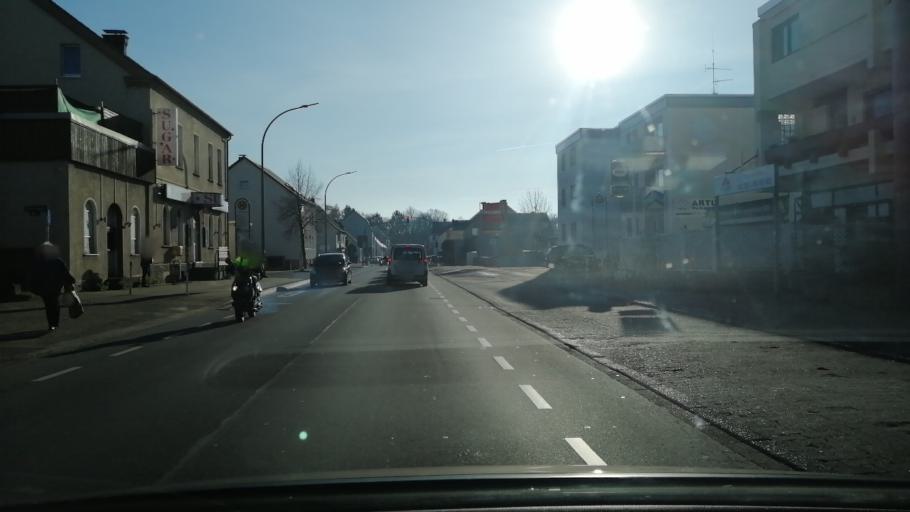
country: DE
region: North Rhine-Westphalia
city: Schwerte
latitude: 51.4999
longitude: 7.5605
